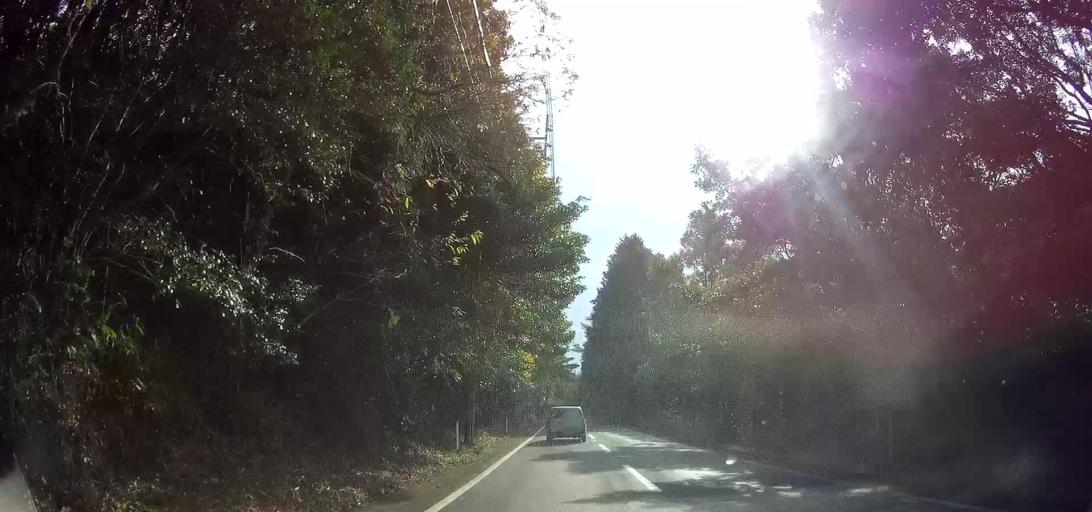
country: JP
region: Nagasaki
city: Shimabara
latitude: 32.6976
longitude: 130.2491
